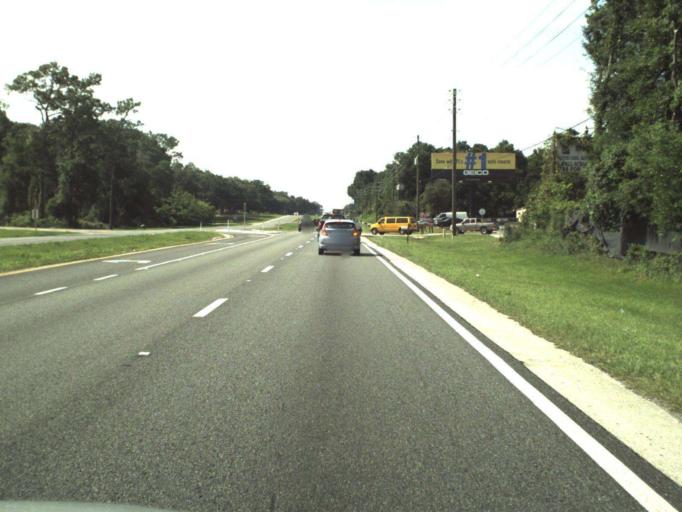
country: US
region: Florida
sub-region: Marion County
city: Belleview
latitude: 29.1153
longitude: -82.0964
